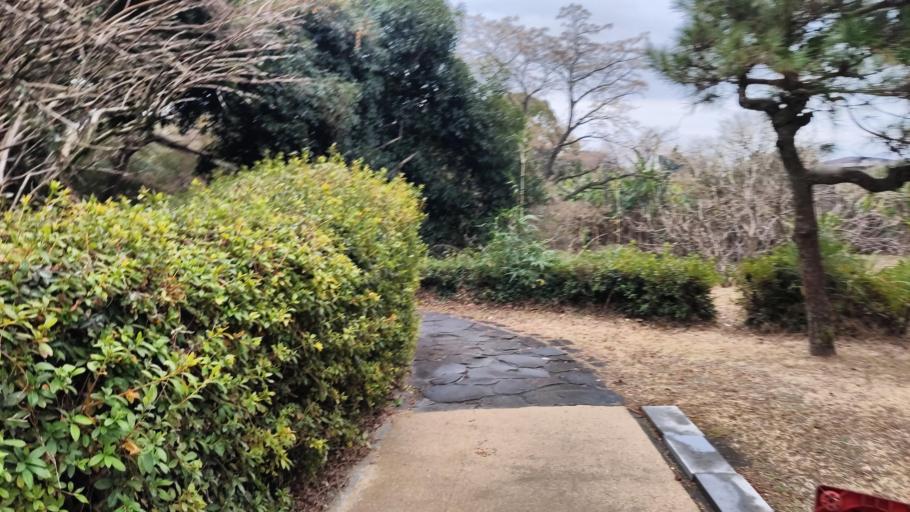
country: JP
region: Kumamoto
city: Kumamoto
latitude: 32.7857
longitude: 130.7350
